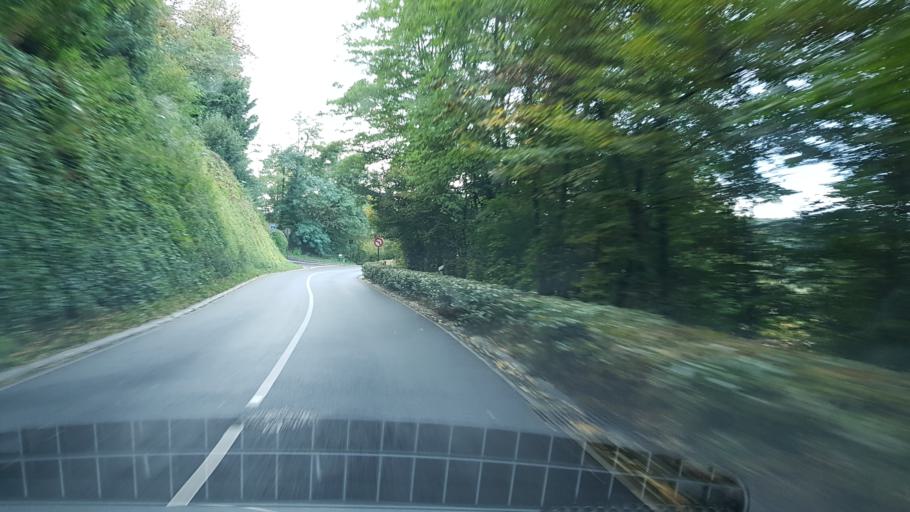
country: FR
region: Ile-de-France
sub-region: Departement de l'Essonne
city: Gif-sur-Yvette
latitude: 48.6946
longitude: 2.1230
